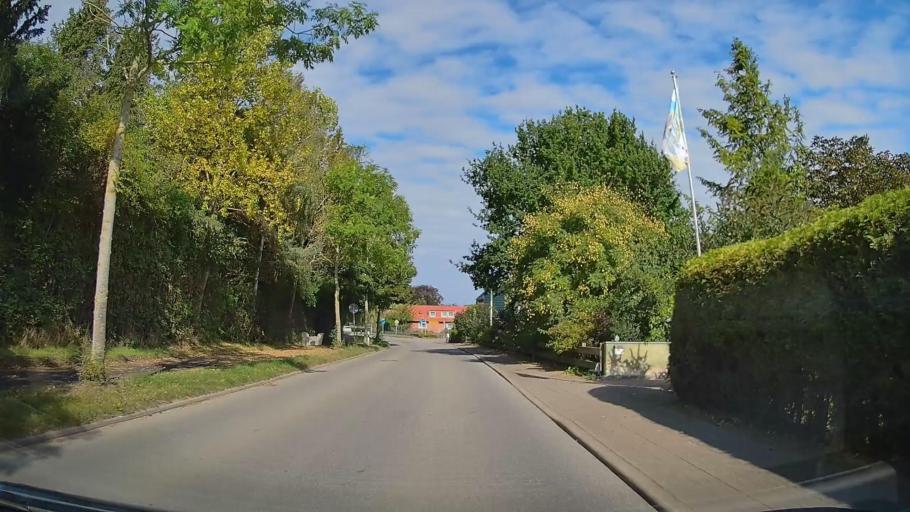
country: DE
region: Schleswig-Holstein
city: Oldenburg in Holstein
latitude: 54.3251
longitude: 10.8917
